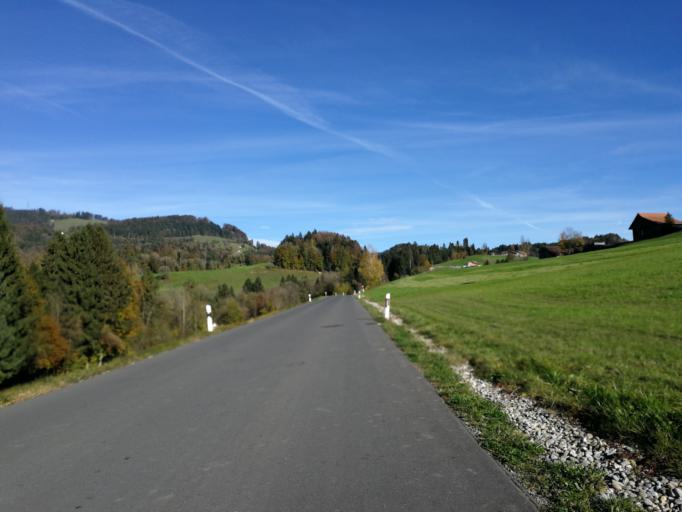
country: CH
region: Saint Gallen
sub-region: Wahlkreis See-Gaster
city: Eschenbach
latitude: 47.2565
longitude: 8.9323
